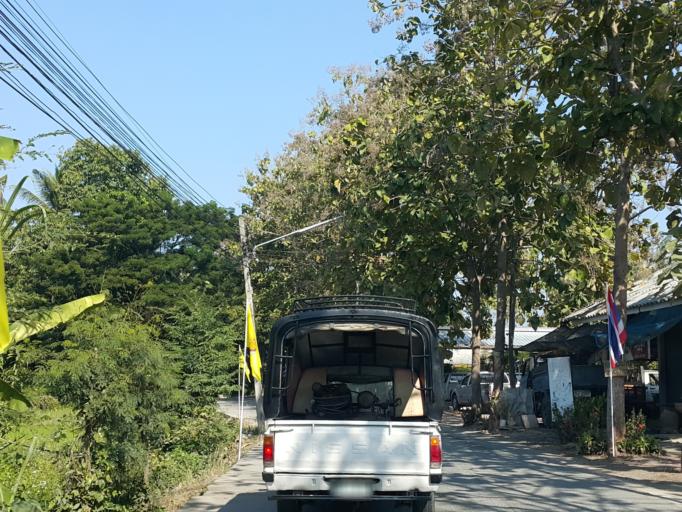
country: TH
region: Chiang Mai
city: San Sai
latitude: 18.8506
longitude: 99.0307
